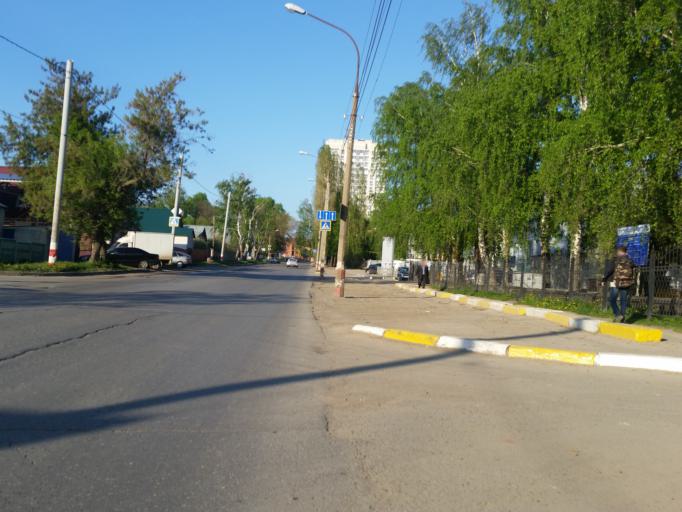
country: RU
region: Ulyanovsk
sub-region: Ulyanovskiy Rayon
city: Ulyanovsk
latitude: 54.3357
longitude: 48.3779
